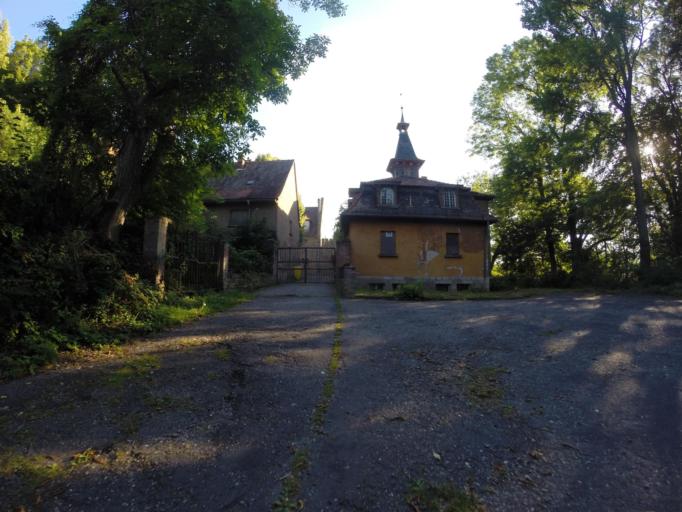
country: DE
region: Thuringia
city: Jena
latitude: 50.9439
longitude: 11.6182
